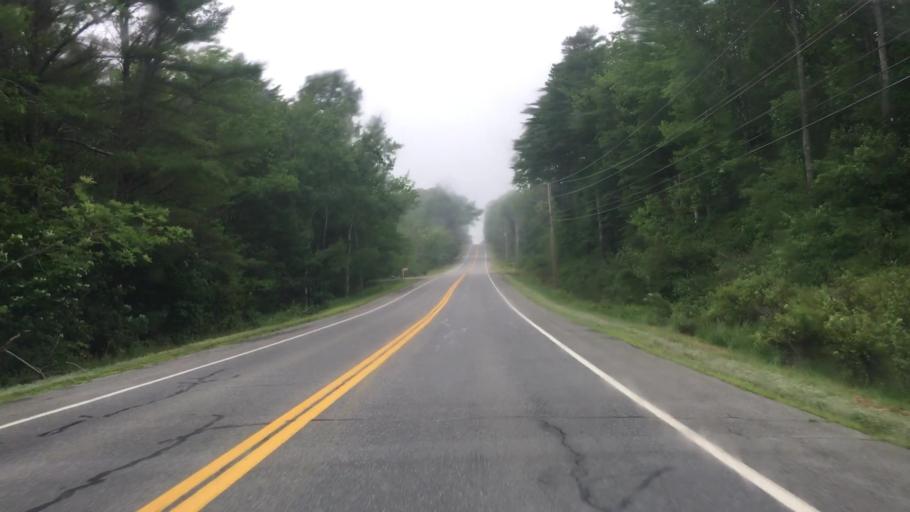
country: US
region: Maine
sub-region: Lincoln County
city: Wiscasset
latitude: 44.0615
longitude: -69.6884
